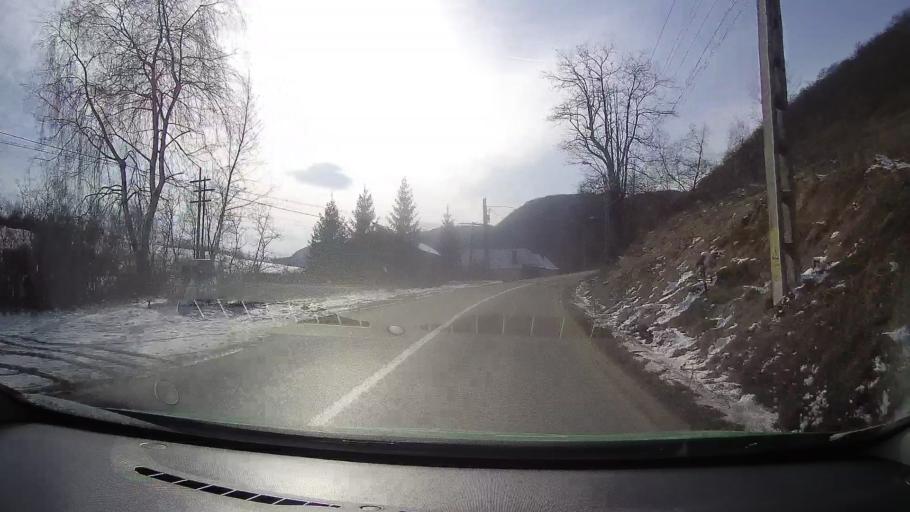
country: RO
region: Mures
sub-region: Municipiul Sighisoara
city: Sighisoara
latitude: 46.2041
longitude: 24.7760
